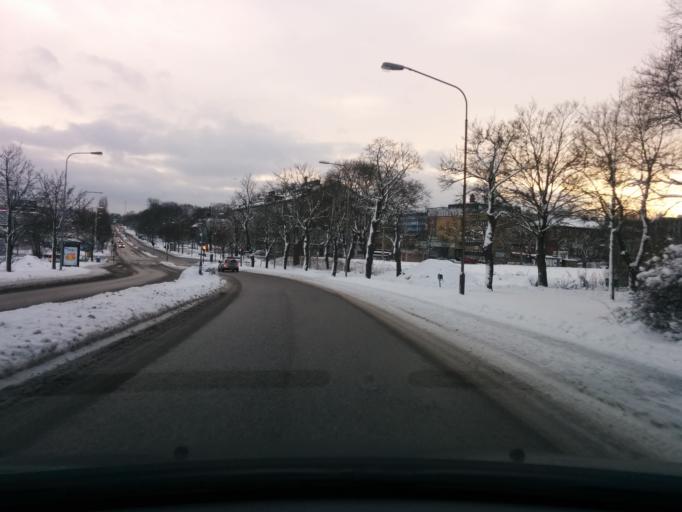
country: SE
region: Stockholm
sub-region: Stockholms Kommun
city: Arsta
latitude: 59.2968
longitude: 18.0114
